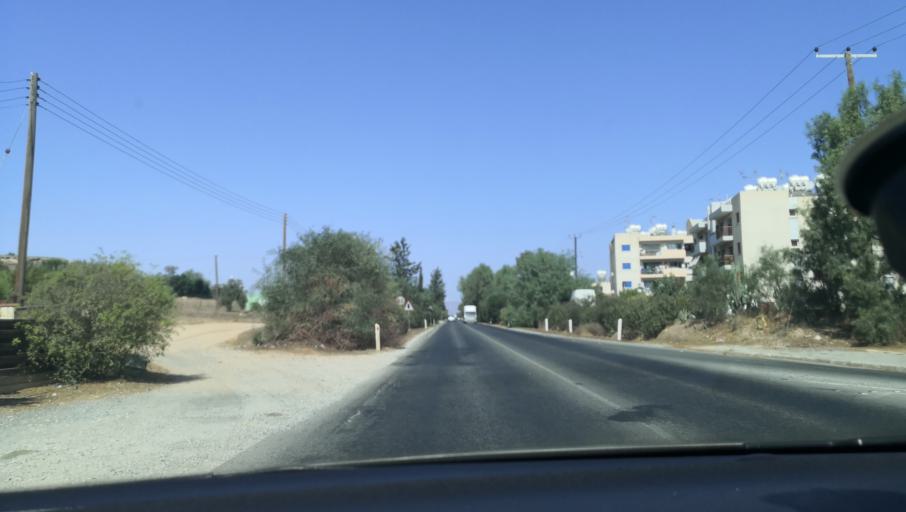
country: CY
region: Lefkosia
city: Kato Deftera
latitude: 35.1014
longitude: 33.2868
